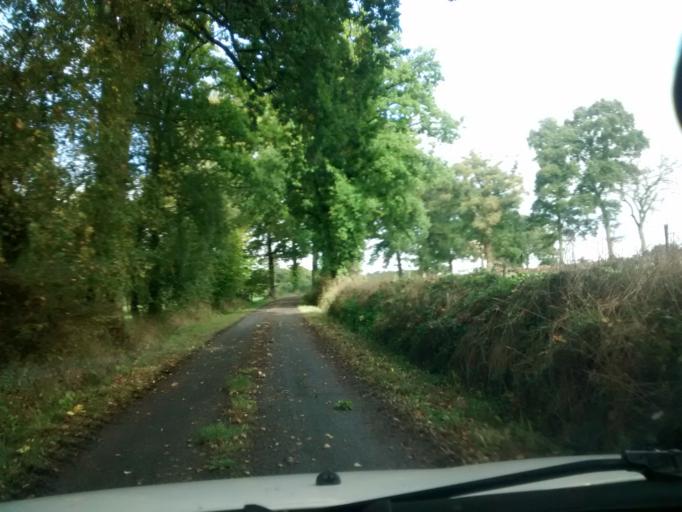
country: FR
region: Brittany
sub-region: Departement d'Ille-et-Vilaine
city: Chateaubourg
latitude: 48.1401
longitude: -1.4254
